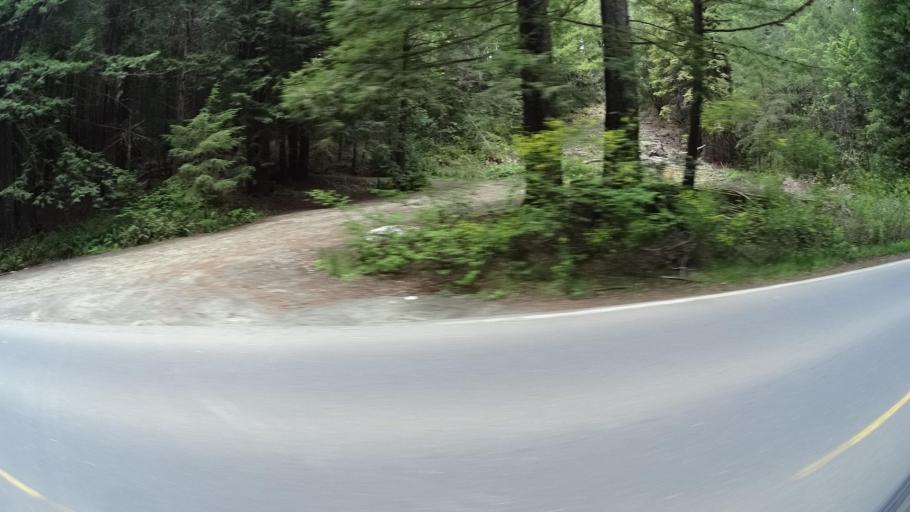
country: US
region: California
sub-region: Humboldt County
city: Redway
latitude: 40.1248
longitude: -123.8455
